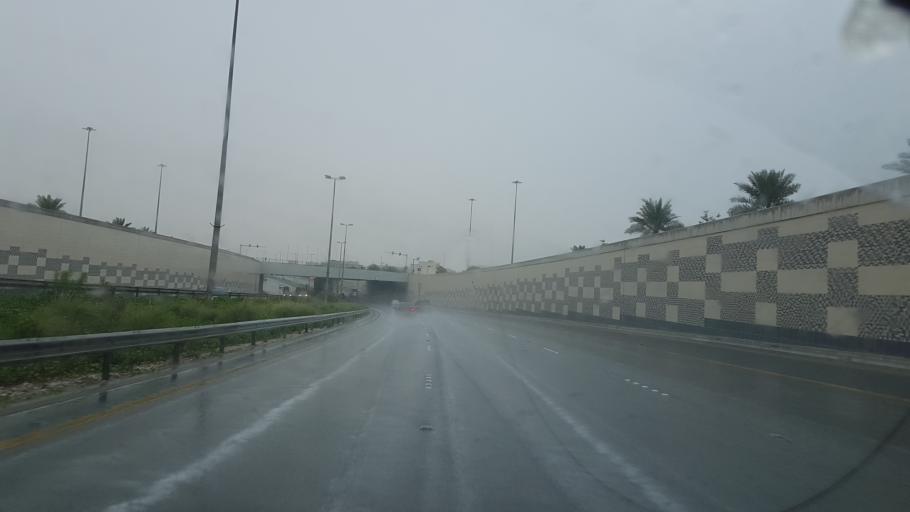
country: BH
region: Central Governorate
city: Madinat Hamad
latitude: 26.1000
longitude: 50.5113
